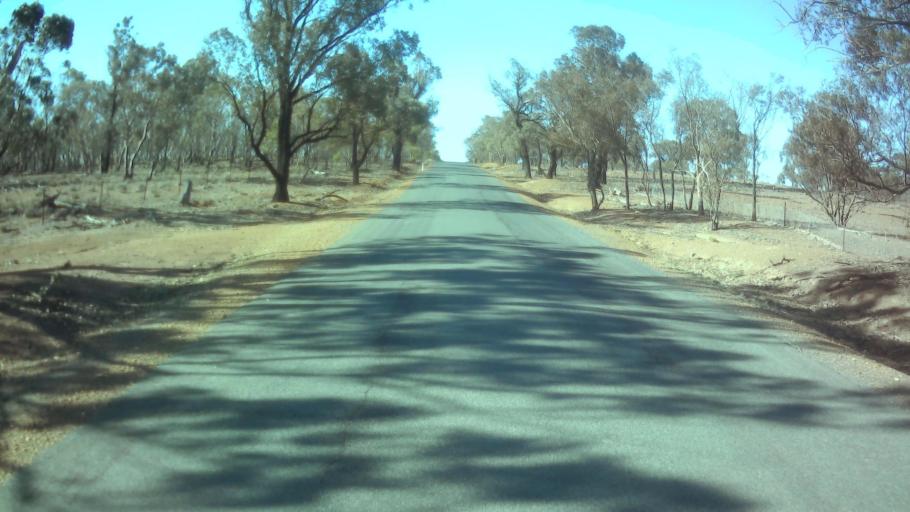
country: AU
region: New South Wales
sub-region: Forbes
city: Forbes
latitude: -33.7065
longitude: 147.8055
